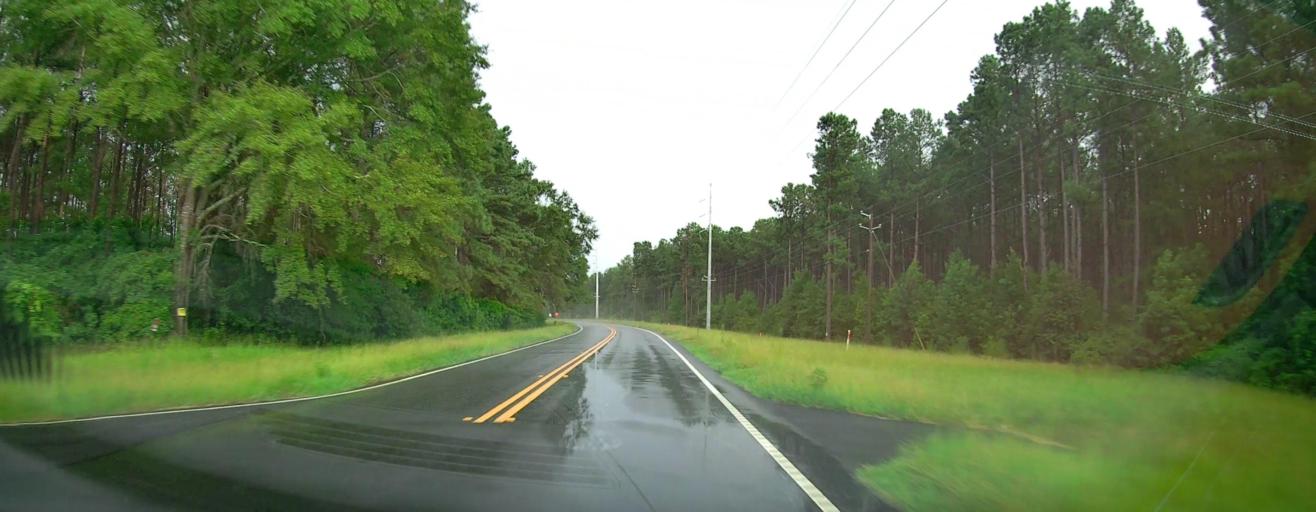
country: US
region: Georgia
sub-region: Twiggs County
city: Jeffersonville
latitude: 32.5849
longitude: -83.2210
